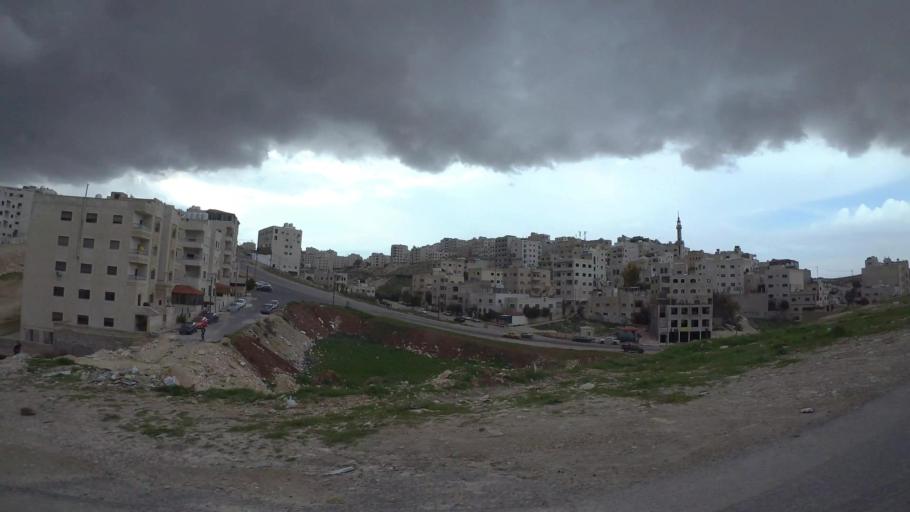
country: JO
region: Amman
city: Amman
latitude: 32.0098
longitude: 35.9470
